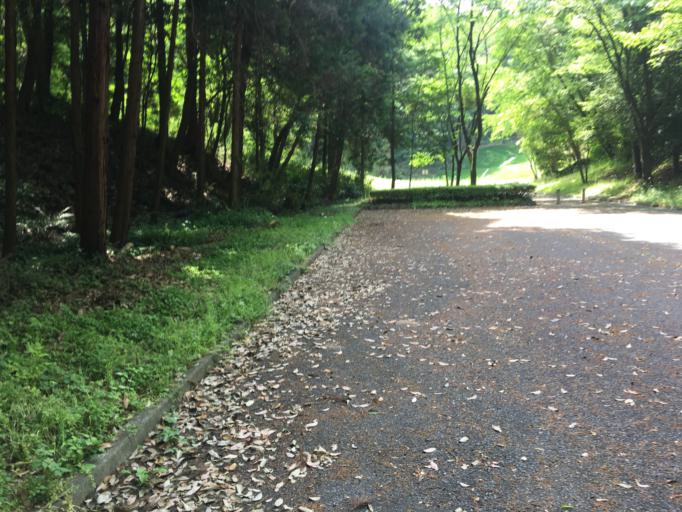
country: JP
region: Saitama
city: Hanno
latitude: 35.8515
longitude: 139.3101
